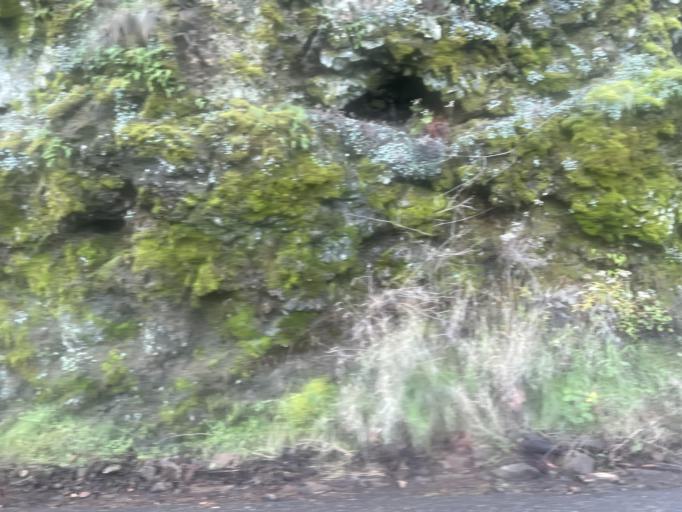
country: US
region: Washington
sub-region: Clark County
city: Washougal
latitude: 45.5463
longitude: -122.1981
